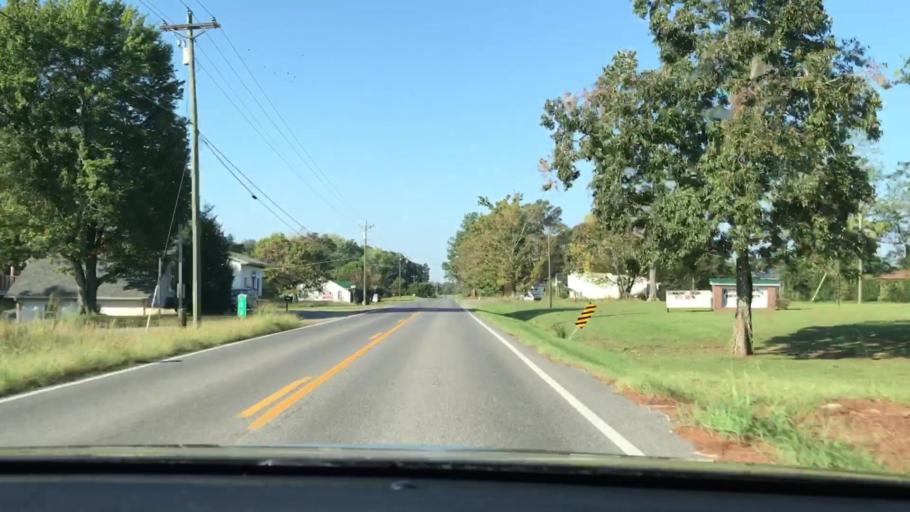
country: US
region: Kentucky
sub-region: Marshall County
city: Benton
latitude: 36.7708
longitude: -88.1723
